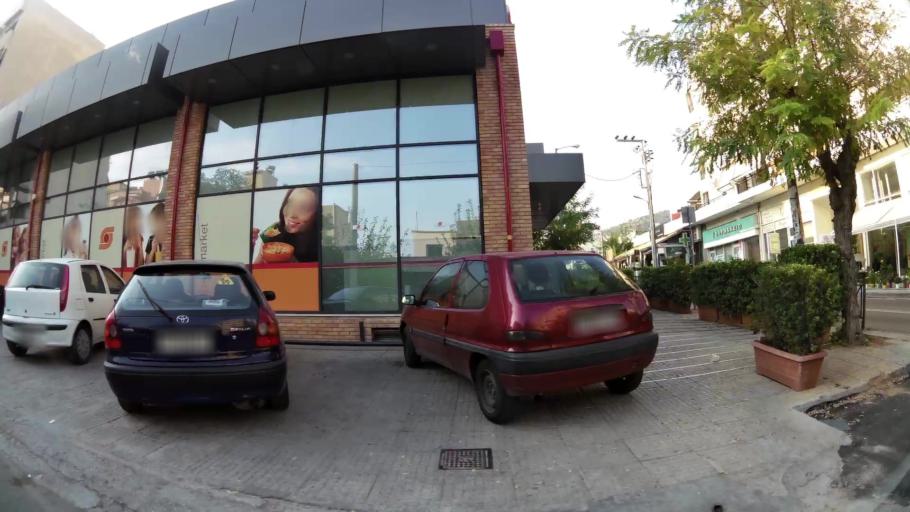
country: GR
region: Attica
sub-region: Nomarchia Athinas
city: Petroupolis
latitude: 38.0378
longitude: 23.6743
